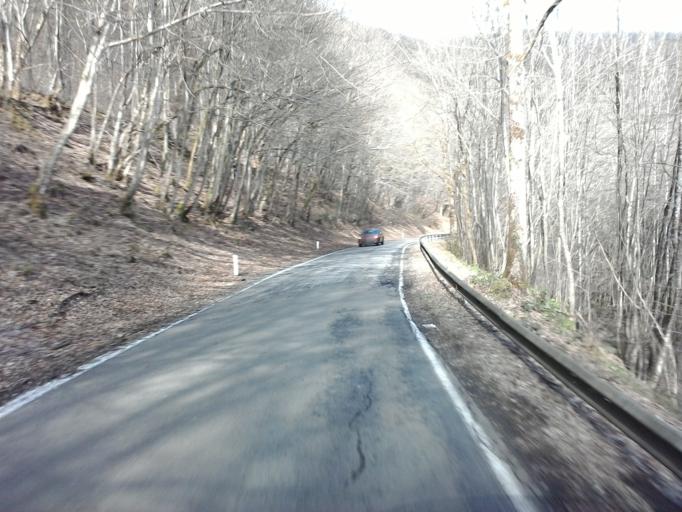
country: BE
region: Wallonia
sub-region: Province du Luxembourg
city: Daverdisse
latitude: 50.0390
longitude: 5.1250
